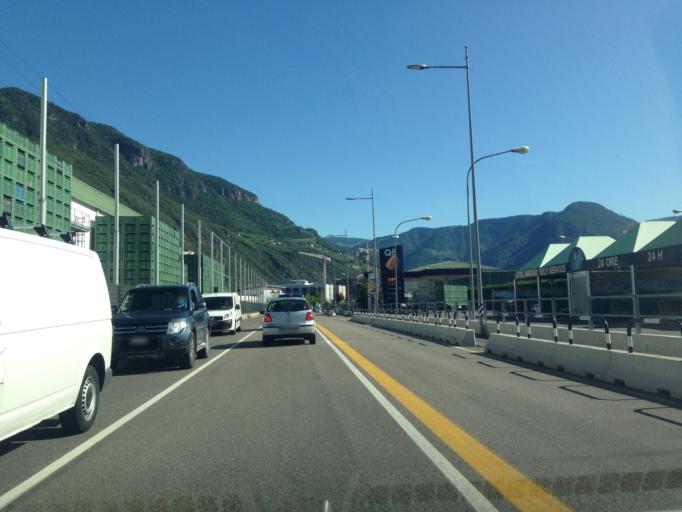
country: IT
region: Trentino-Alto Adige
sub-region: Bolzano
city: Bolzano
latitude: 46.4907
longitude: 11.3056
